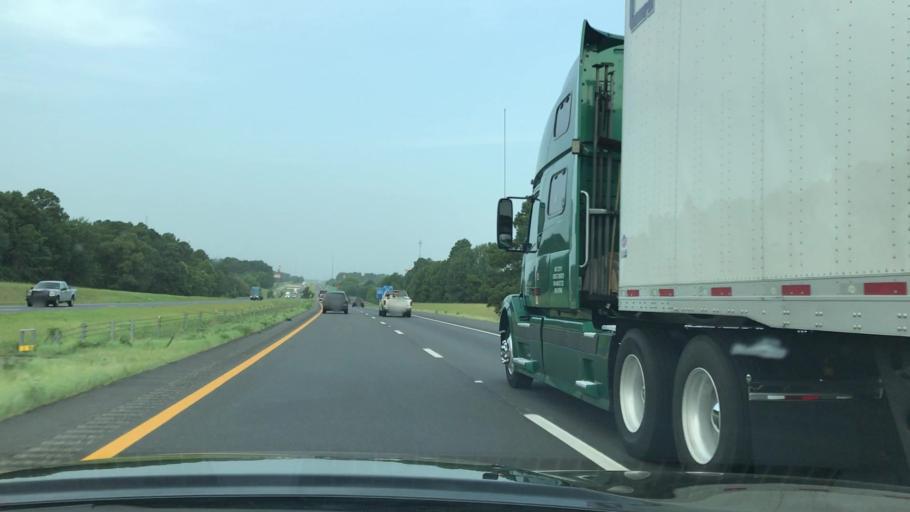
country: US
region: Texas
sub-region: Gregg County
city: Longview
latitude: 32.4559
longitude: -94.6928
